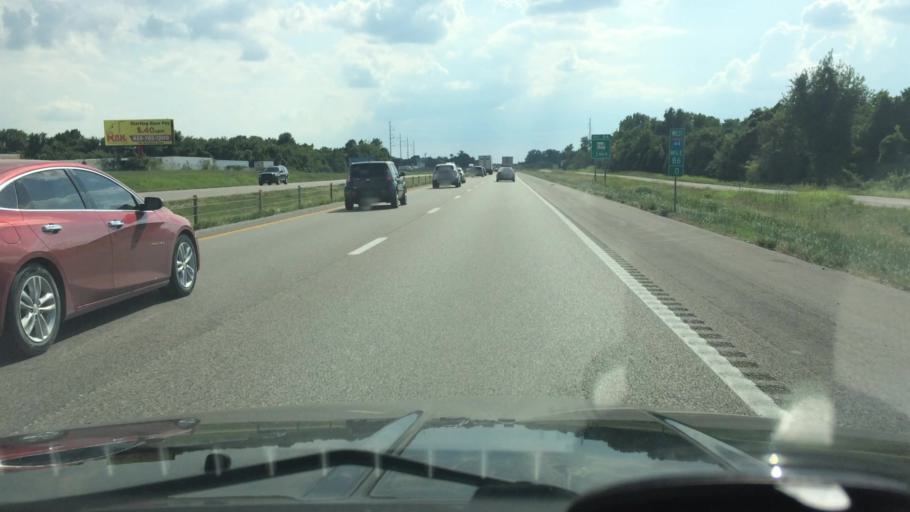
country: US
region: Missouri
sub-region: Greene County
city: Strafford
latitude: 37.2573
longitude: -93.1628
